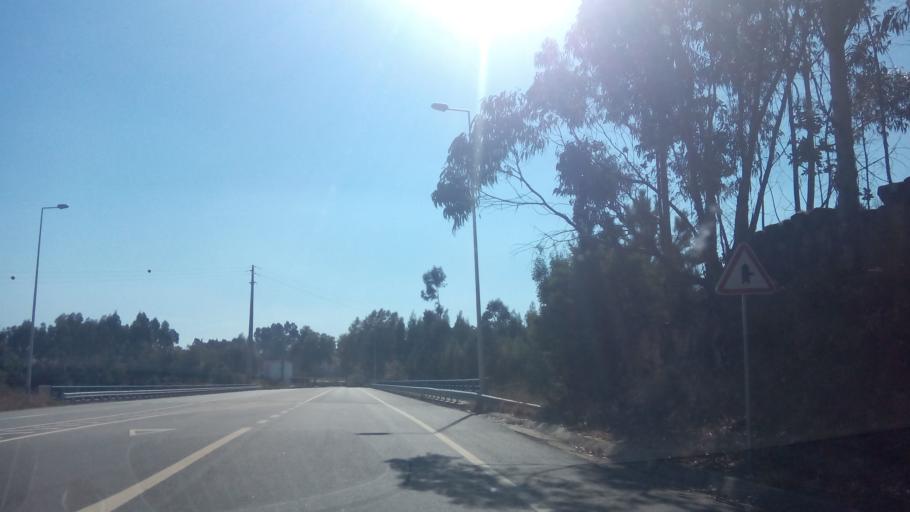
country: PT
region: Porto
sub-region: Lousada
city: Meinedo
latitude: 41.2478
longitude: -8.2160
